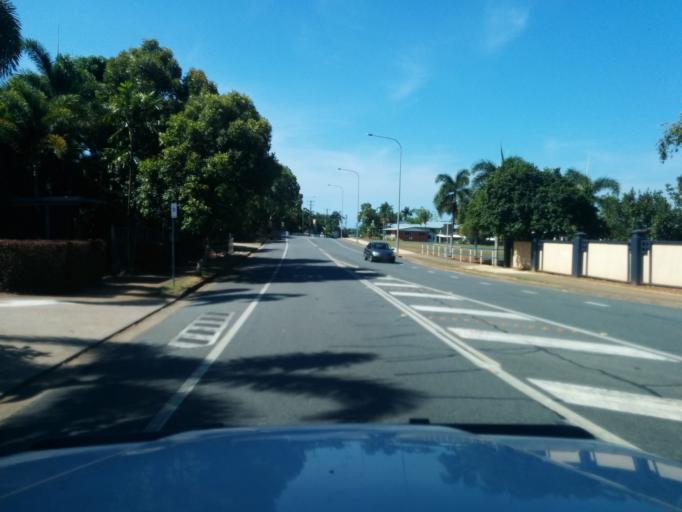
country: AU
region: Queensland
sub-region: Cairns
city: Redlynch
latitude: -16.8910
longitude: 145.6958
